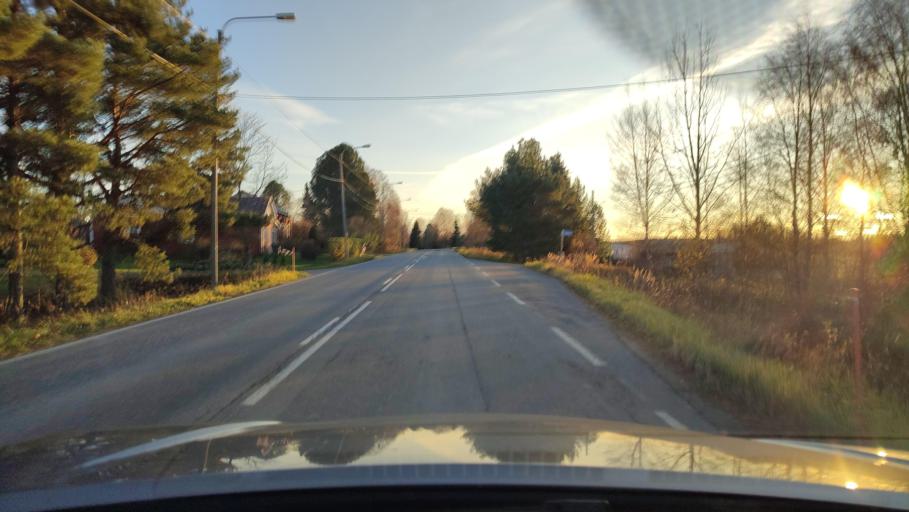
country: FI
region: Ostrobothnia
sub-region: Sydosterbotten
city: Naerpes
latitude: 62.4966
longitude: 21.3454
